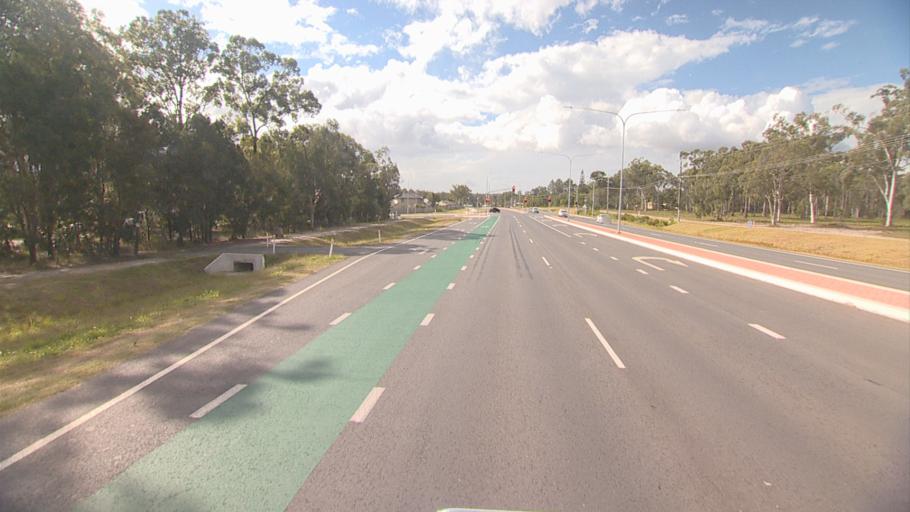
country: AU
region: Queensland
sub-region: Logan
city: Logan Reserve
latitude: -27.7013
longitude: 153.0983
